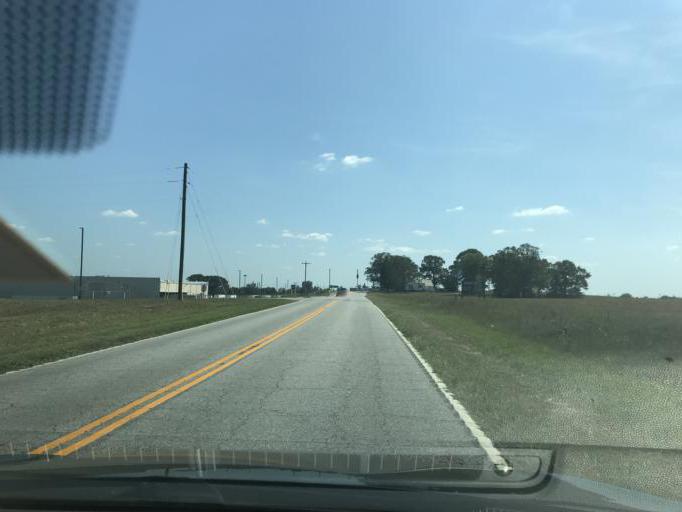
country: US
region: South Carolina
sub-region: Cherokee County
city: Gaffney
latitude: 35.0889
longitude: -81.7102
